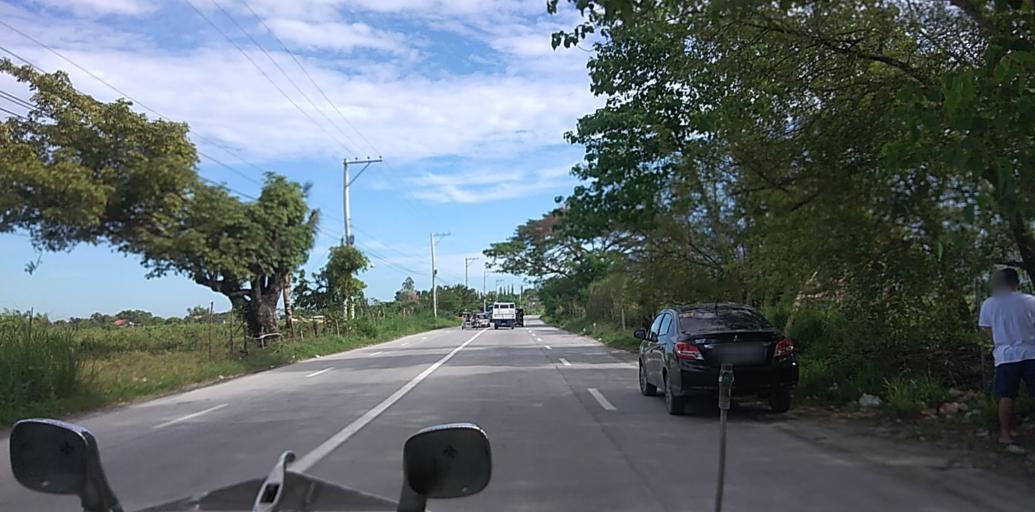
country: PH
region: Central Luzon
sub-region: Province of Pampanga
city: Malino
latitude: 15.1219
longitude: 120.6669
